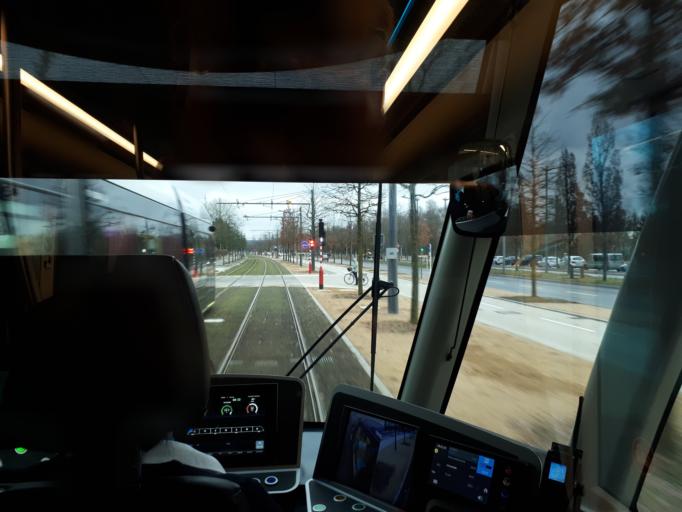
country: LU
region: Luxembourg
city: Kirchberg
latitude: 49.6233
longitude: 6.1555
